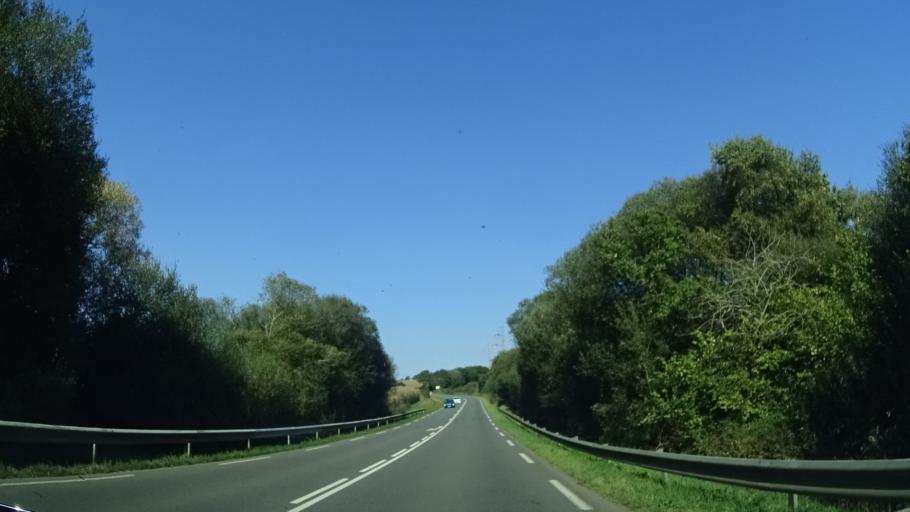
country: FR
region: Brittany
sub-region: Departement du Finistere
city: Plonevez-Porzay
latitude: 48.1115
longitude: -4.2416
